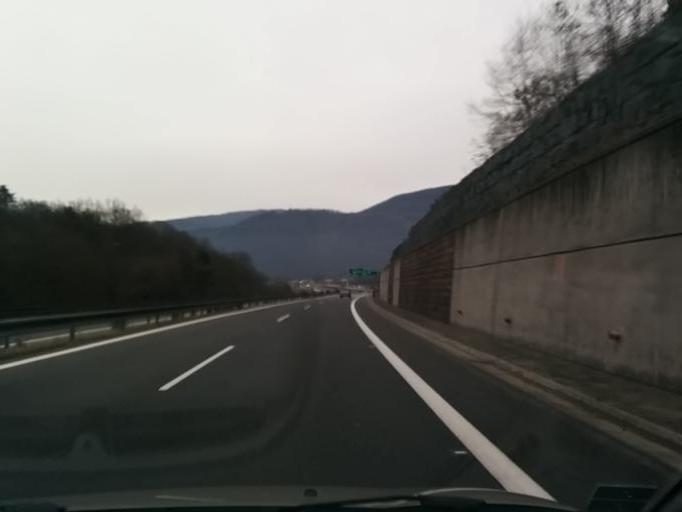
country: SK
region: Nitriansky
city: Tlmace
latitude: 48.3633
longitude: 18.5694
